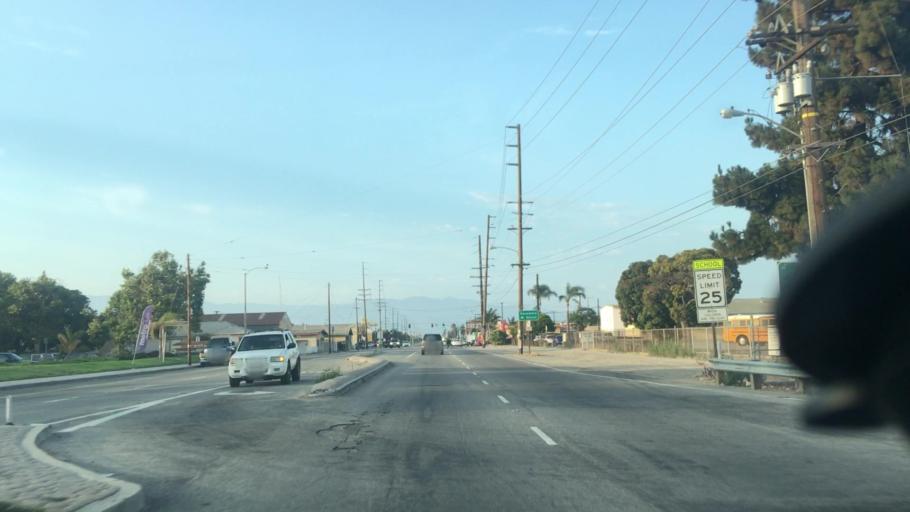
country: US
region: California
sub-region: Ventura County
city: El Rio
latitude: 34.2349
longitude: -119.1710
